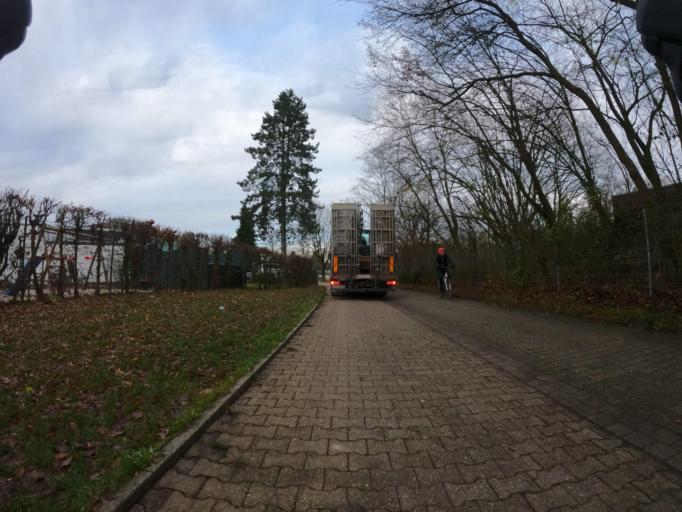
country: DE
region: North Rhine-Westphalia
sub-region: Regierungsbezirk Koln
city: Wurselen
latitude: 50.7516
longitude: 6.1513
